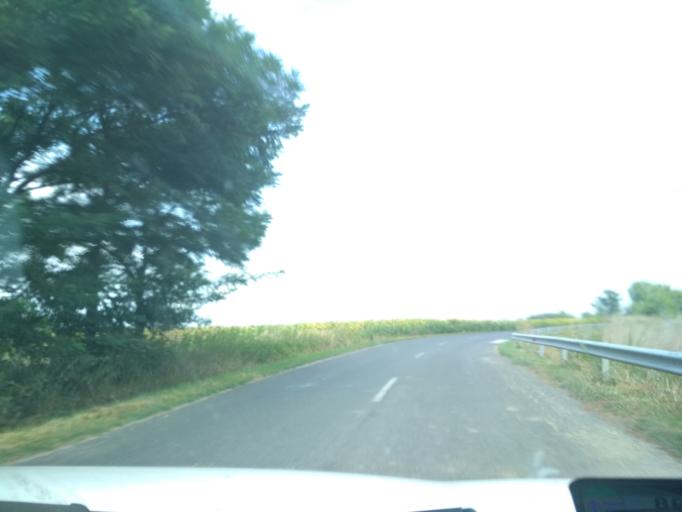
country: HU
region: Jasz-Nagykun-Szolnok
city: Tiszaszolos
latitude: 47.5309
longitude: 20.6972
